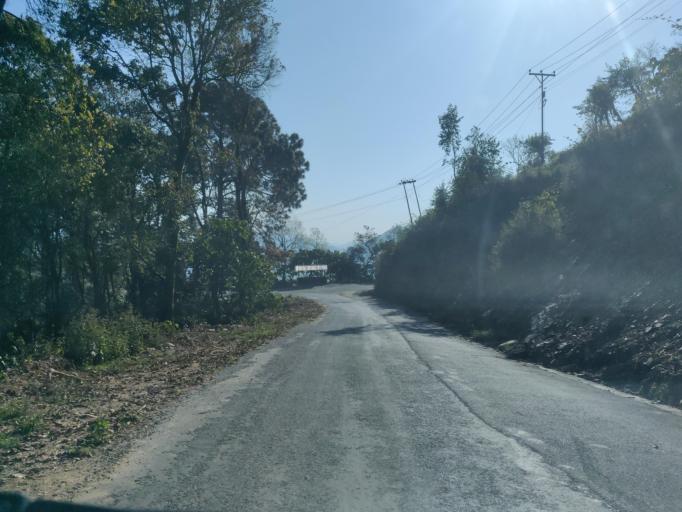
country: NP
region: Western Region
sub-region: Gandaki Zone
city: Pokhara
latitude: 28.2448
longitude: 83.9630
